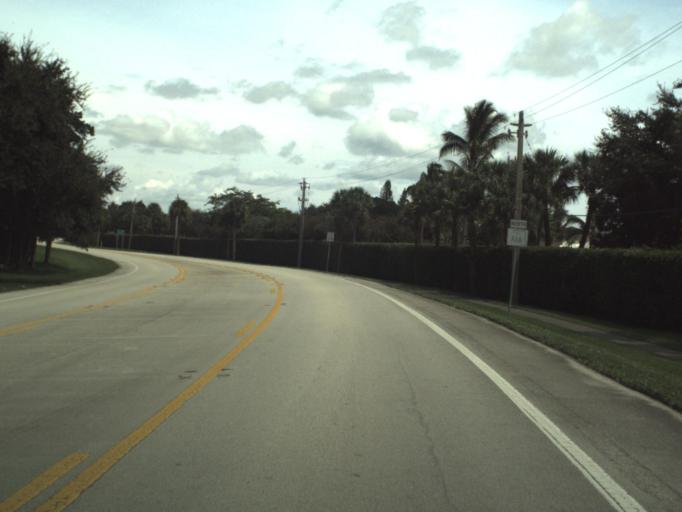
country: US
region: Florida
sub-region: Palm Beach County
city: North Palm Beach
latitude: 26.8367
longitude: -80.0488
